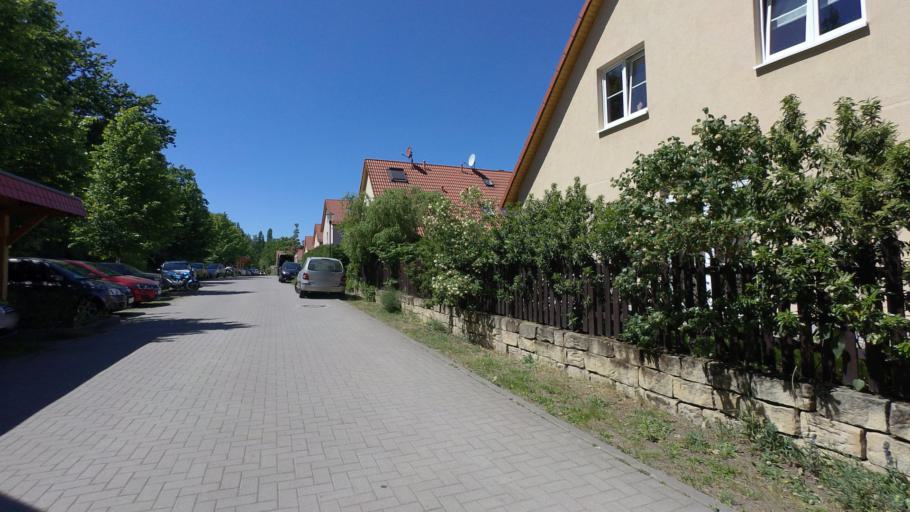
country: DE
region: Berlin
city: Wittenau
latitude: 52.5781
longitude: 13.3227
